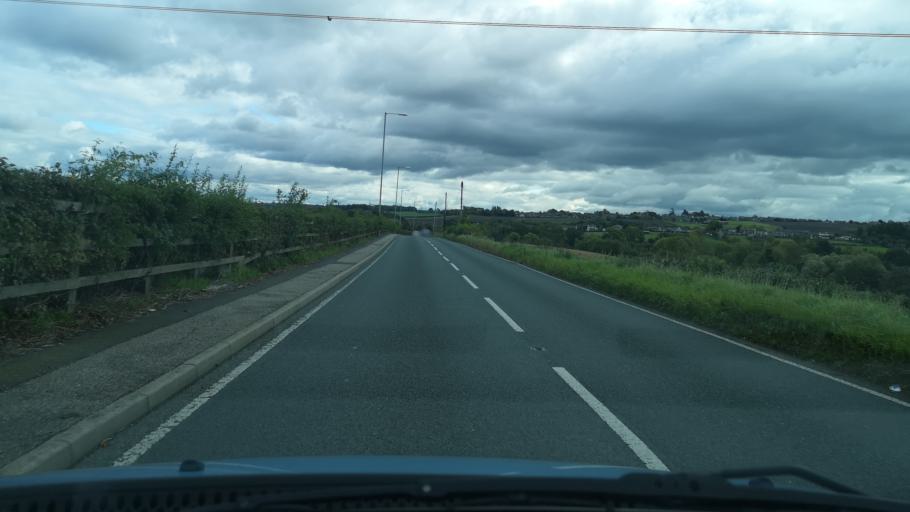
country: GB
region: England
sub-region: City and Borough of Wakefield
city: Middlestown
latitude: 53.6601
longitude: -1.5901
